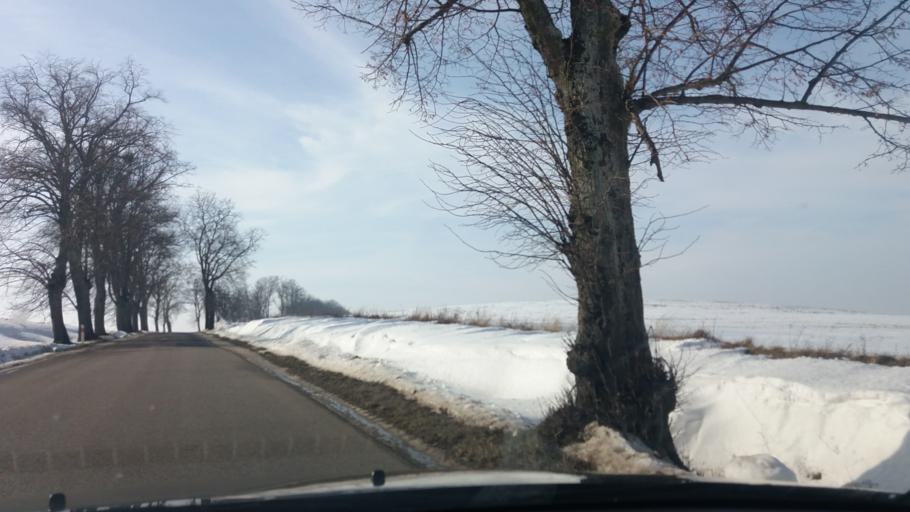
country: PL
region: Warmian-Masurian Voivodeship
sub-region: Powiat bartoszycki
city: Bisztynek
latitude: 54.1128
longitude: 20.8504
